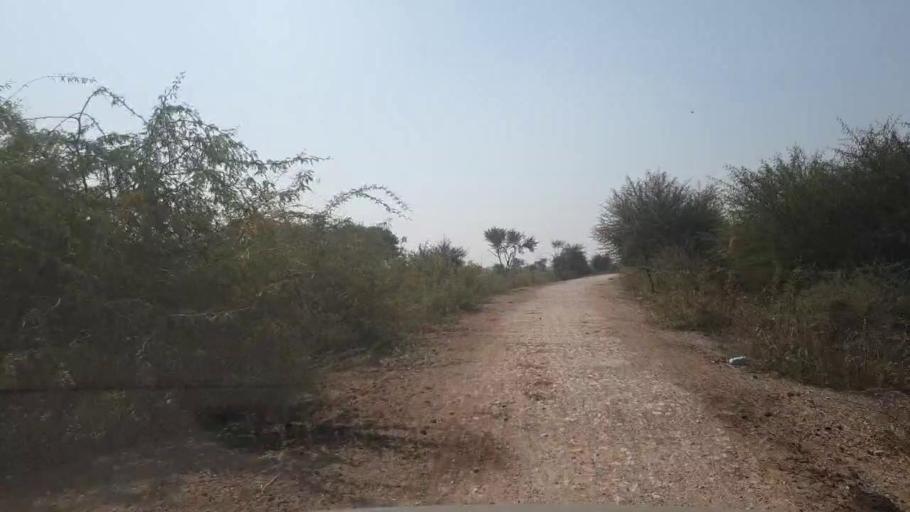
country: PK
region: Sindh
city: Chambar
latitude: 25.2318
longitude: 68.8221
